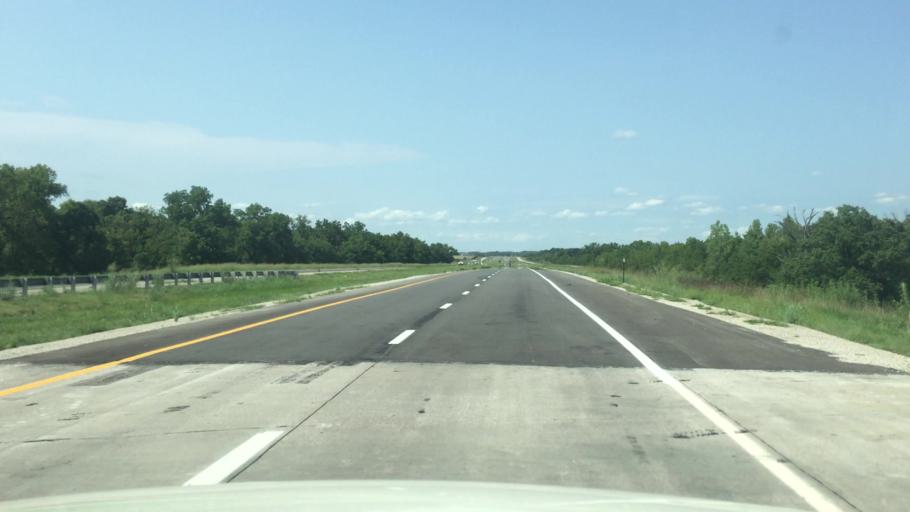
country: US
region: Kansas
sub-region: Linn County
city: La Cygne
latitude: 38.3003
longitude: -94.6773
